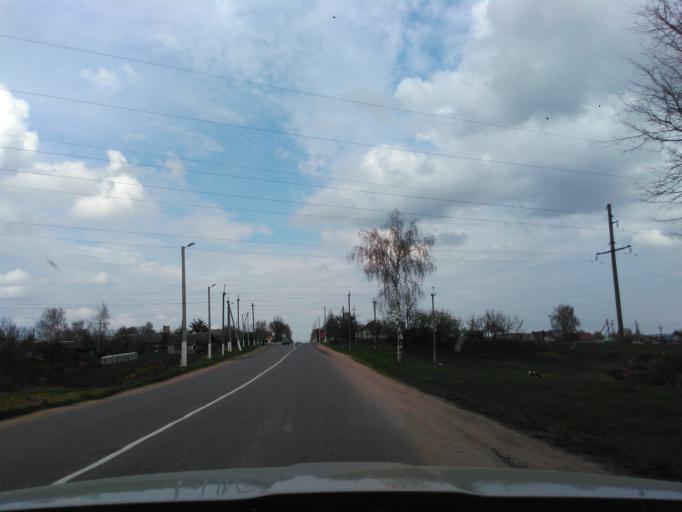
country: BY
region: Vitebsk
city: Chashniki
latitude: 54.8414
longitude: 29.1778
